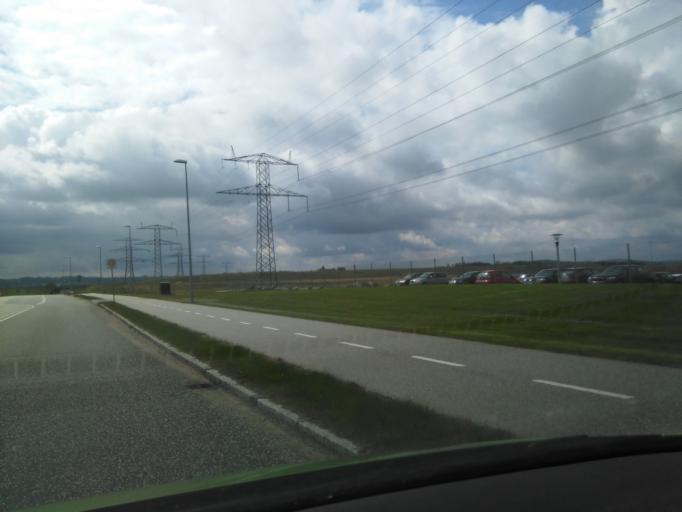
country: DK
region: Central Jutland
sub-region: Arhus Kommune
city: Framlev
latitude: 56.1614
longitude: 10.0597
